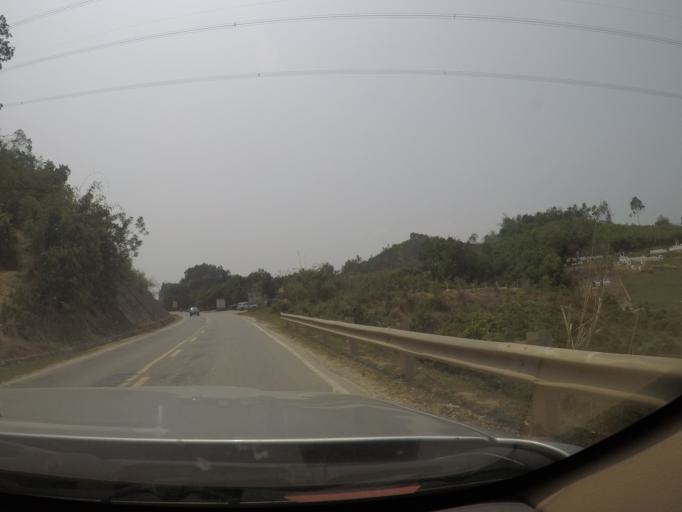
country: VN
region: Thanh Hoa
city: Thi Tran Yen Cat
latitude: 19.6679
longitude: 105.4307
